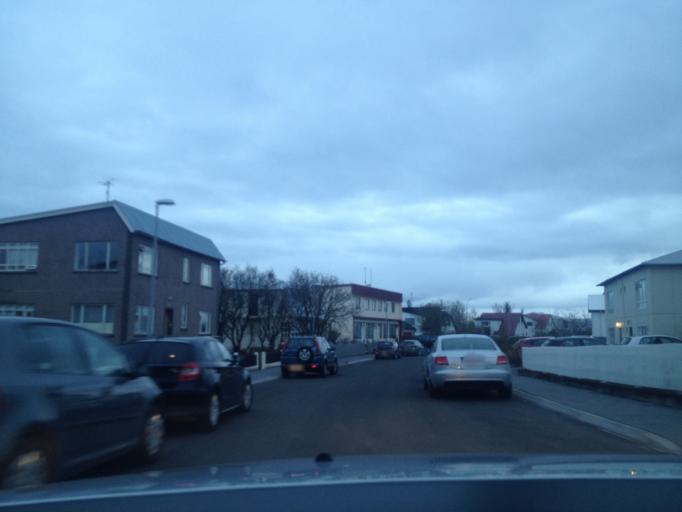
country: IS
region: Capital Region
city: Seltjarnarnes
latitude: 64.1532
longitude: -22.0001
